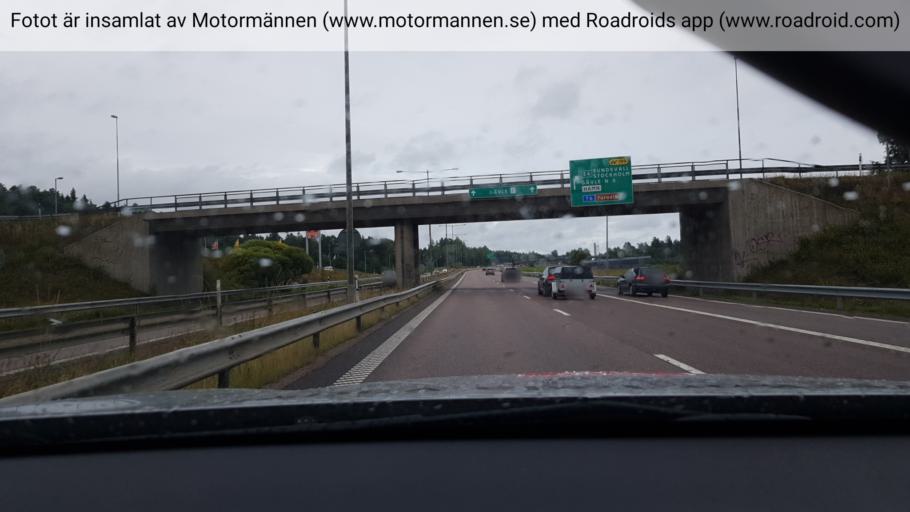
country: SE
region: Gaevleborg
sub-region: Gavle Kommun
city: Valbo
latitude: 60.6662
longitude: 17.0762
